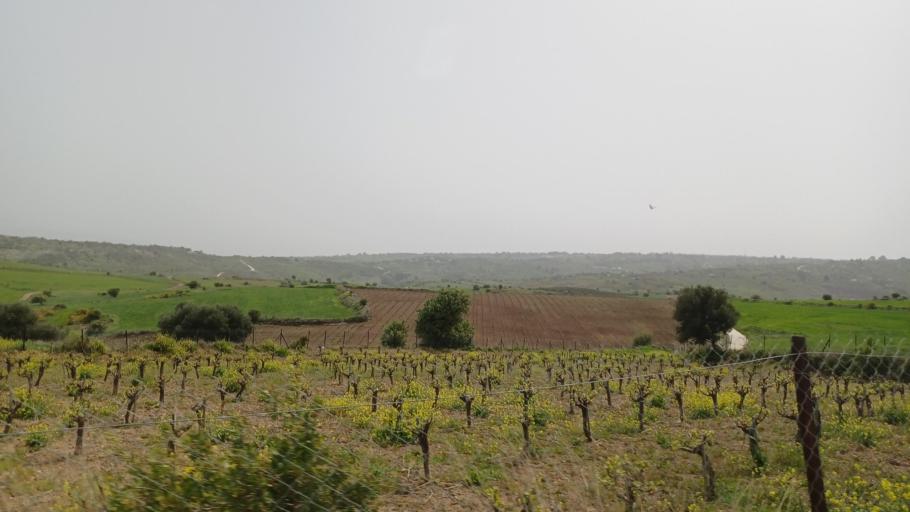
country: CY
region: Pafos
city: Polis
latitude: 34.9910
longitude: 32.3879
